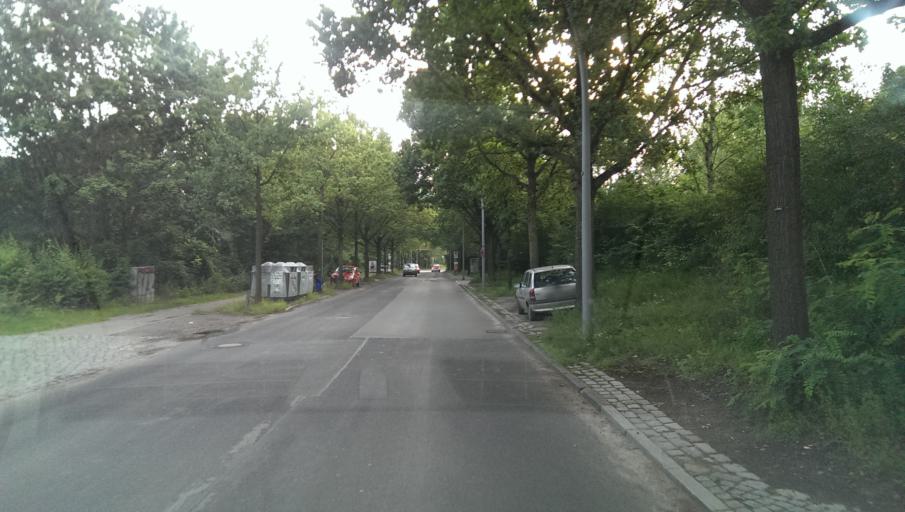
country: DE
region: Berlin
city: Lichterfelde
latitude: 52.4106
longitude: 13.3248
